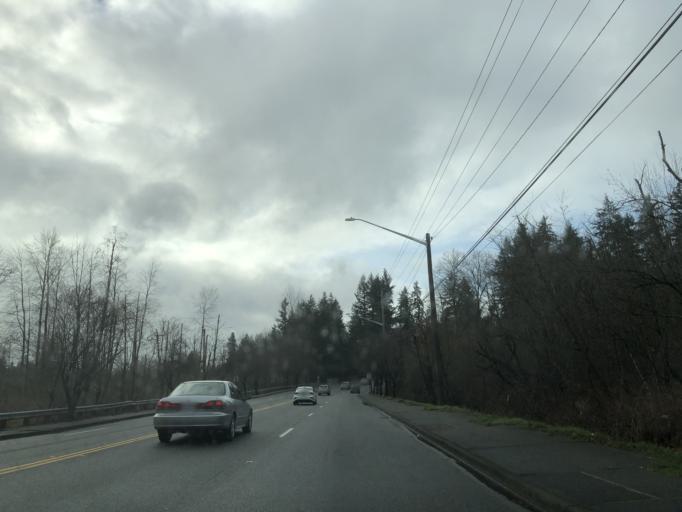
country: US
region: Washington
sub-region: King County
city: Fairwood
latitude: 47.4462
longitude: -122.1647
